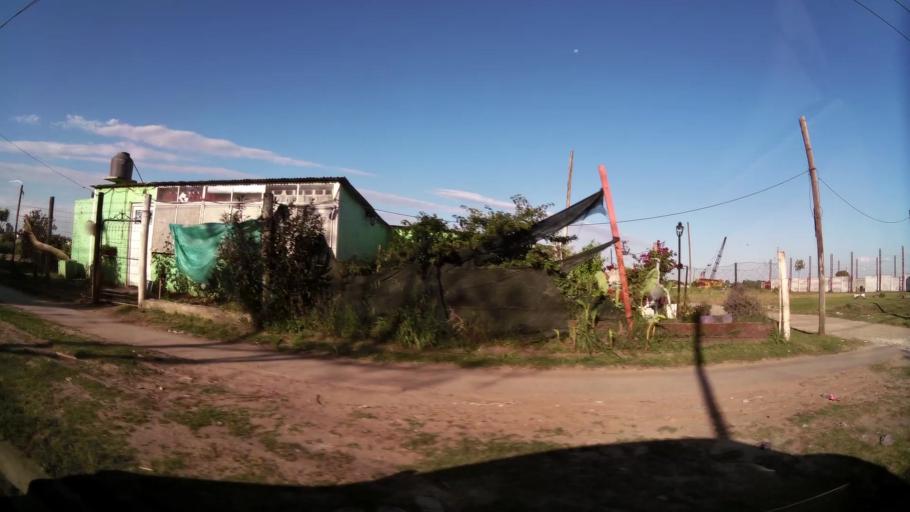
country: AR
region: Buenos Aires
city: Santa Catalina - Dique Lujan
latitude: -34.4747
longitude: -58.7356
